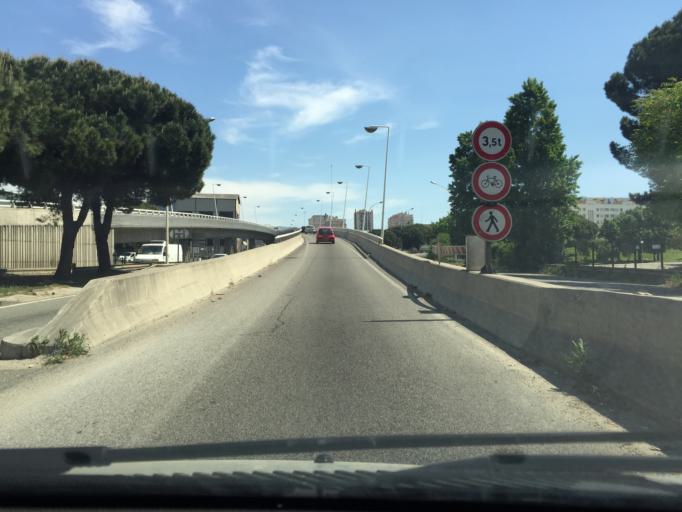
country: FR
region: Provence-Alpes-Cote d'Azur
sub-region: Departement des Bouches-du-Rhone
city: Marseille 03
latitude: 43.3199
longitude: 5.3778
